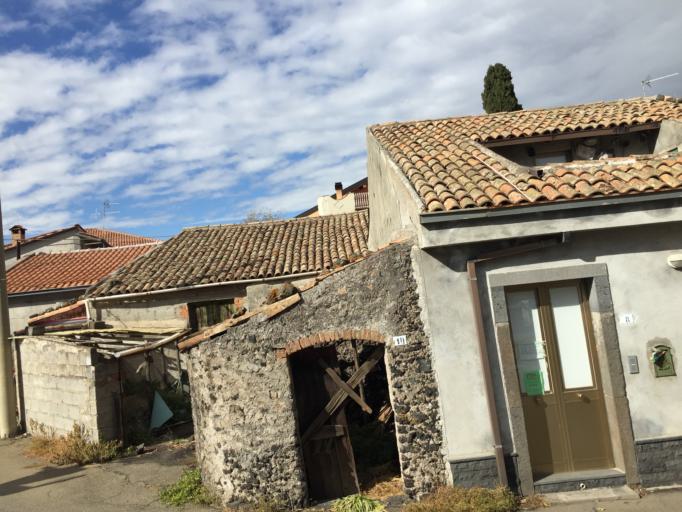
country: IT
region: Sicily
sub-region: Messina
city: Moio Alcantara
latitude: 37.8710
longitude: 15.0389
